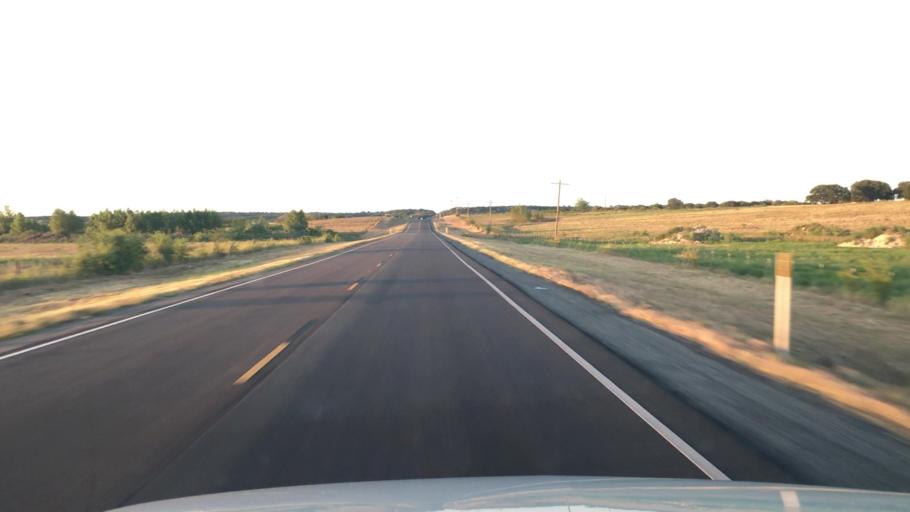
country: US
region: Texas
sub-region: Hamilton County
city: Hico
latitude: 32.0782
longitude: -97.9815
